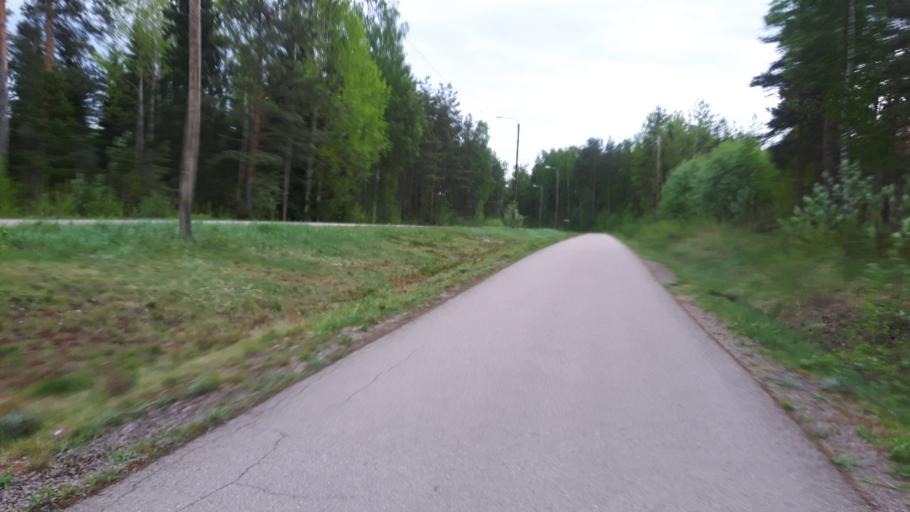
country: FI
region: Kymenlaakso
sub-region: Kotka-Hamina
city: Hamina
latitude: 60.5553
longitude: 27.2288
